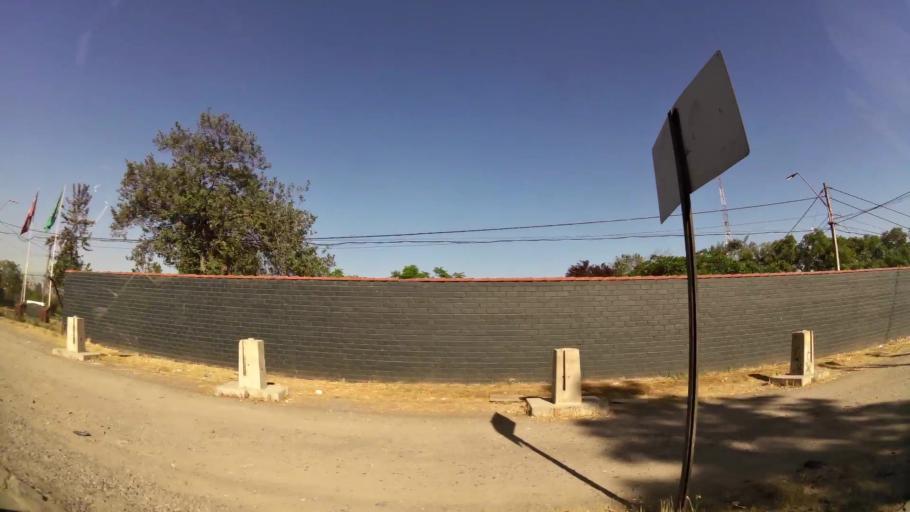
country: CL
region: Santiago Metropolitan
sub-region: Provincia de Maipo
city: San Bernardo
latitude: -33.5488
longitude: -70.6899
